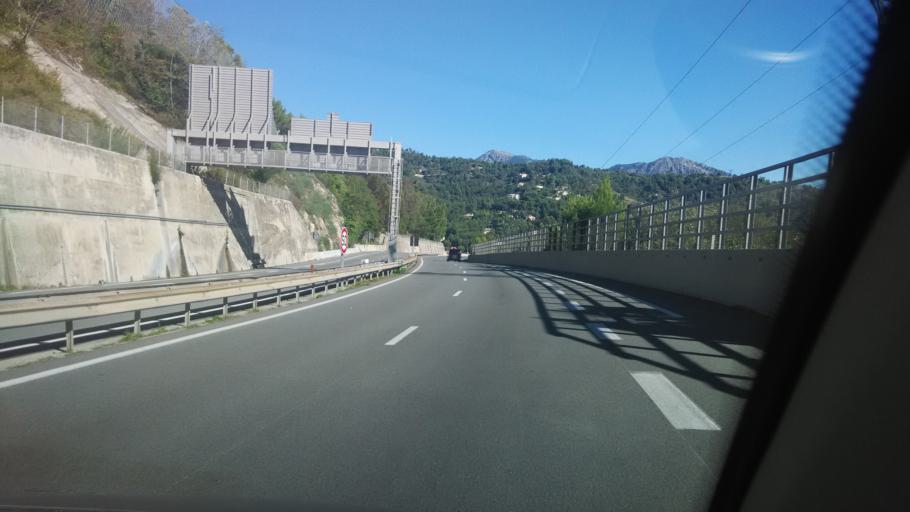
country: MC
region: Commune de Monaco
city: Saint-Roman
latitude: 43.7616
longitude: 7.4471
